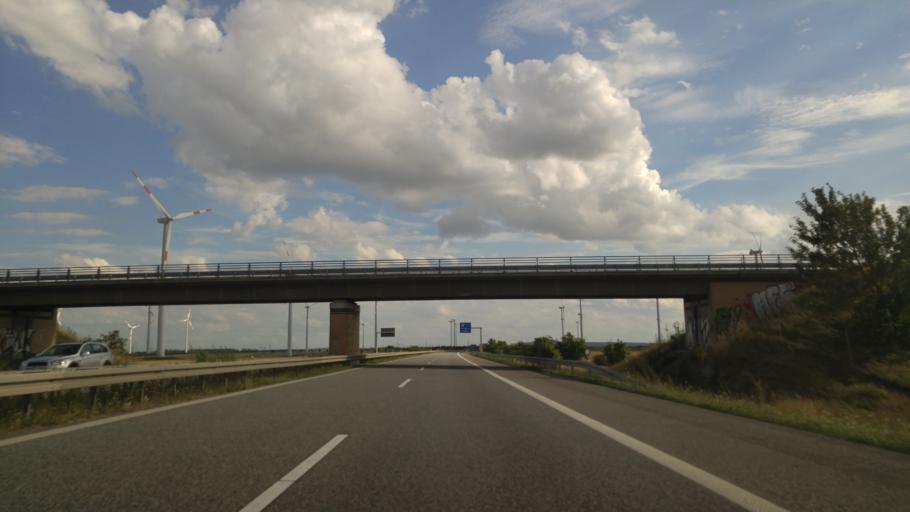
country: DE
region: Saxony-Anhalt
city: Zscherben
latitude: 51.4413
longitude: 11.8644
